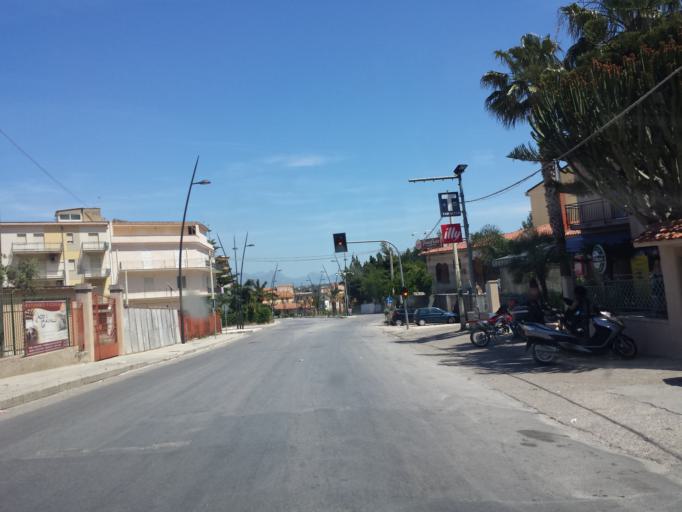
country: IT
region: Sicily
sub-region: Trapani
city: Castellammare del Golfo
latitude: 38.0175
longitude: 12.8863
